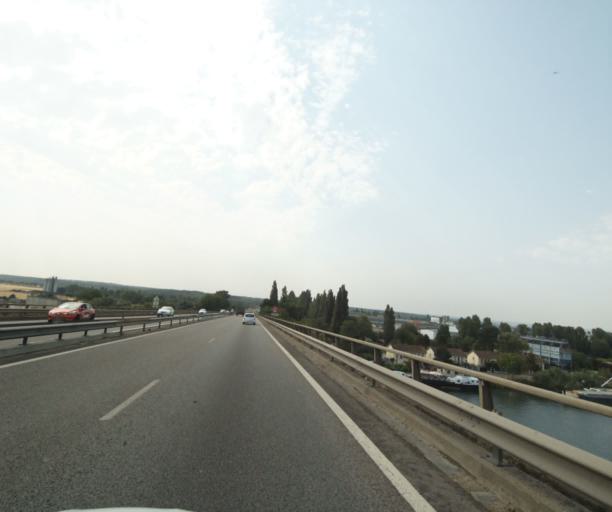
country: FR
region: Ile-de-France
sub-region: Departement des Yvelines
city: Conflans-Sainte-Honorine
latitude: 48.9892
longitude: 2.0823
